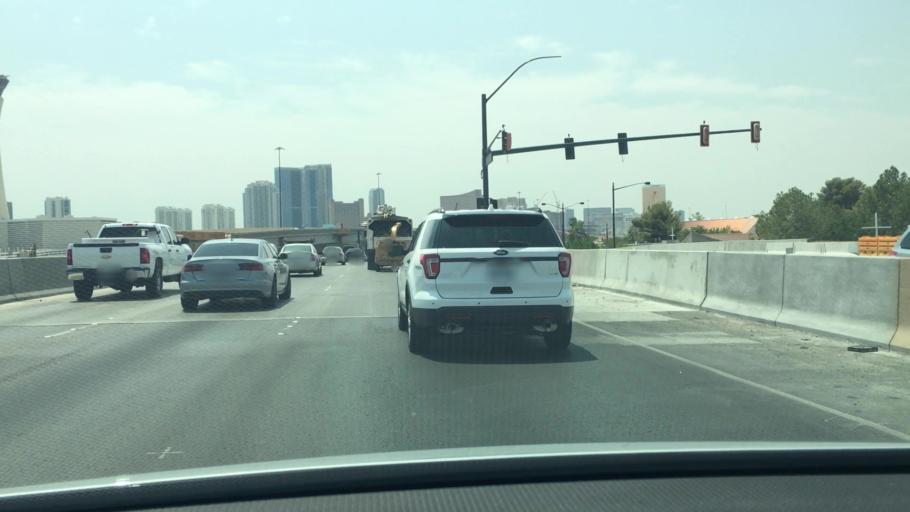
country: US
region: Nevada
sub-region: Clark County
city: Las Vegas
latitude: 36.1595
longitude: -115.1615
